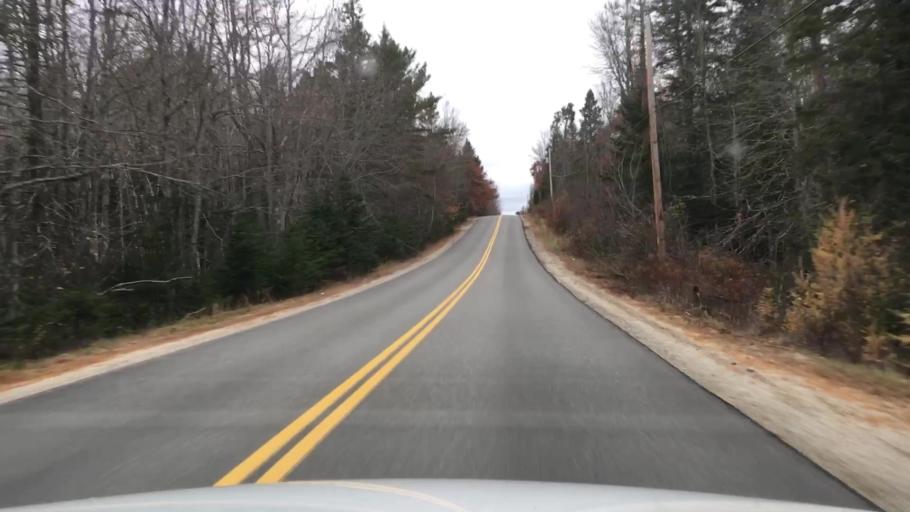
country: US
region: Maine
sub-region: Hancock County
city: Penobscot
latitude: 44.4510
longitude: -68.6371
